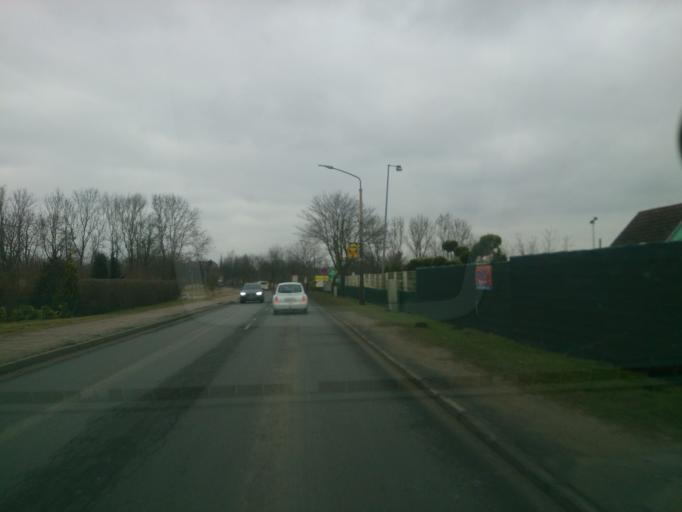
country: DE
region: Mecklenburg-Vorpommern
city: Demmin
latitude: 53.8948
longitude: 13.0403
